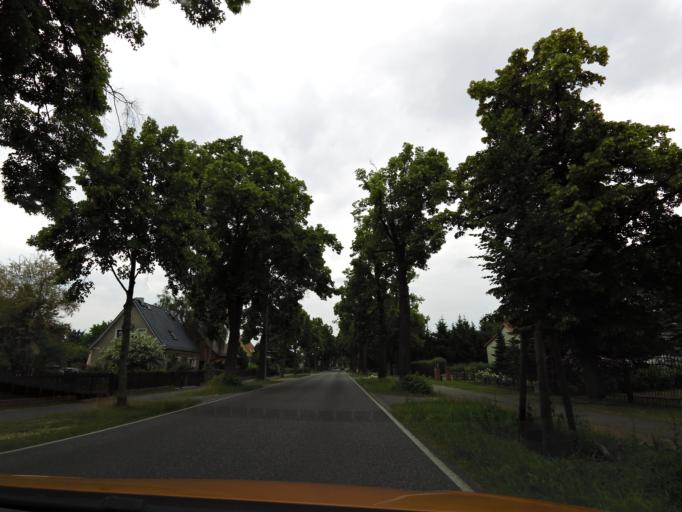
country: DE
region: Brandenburg
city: Zossen
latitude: 52.2027
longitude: 13.4566
